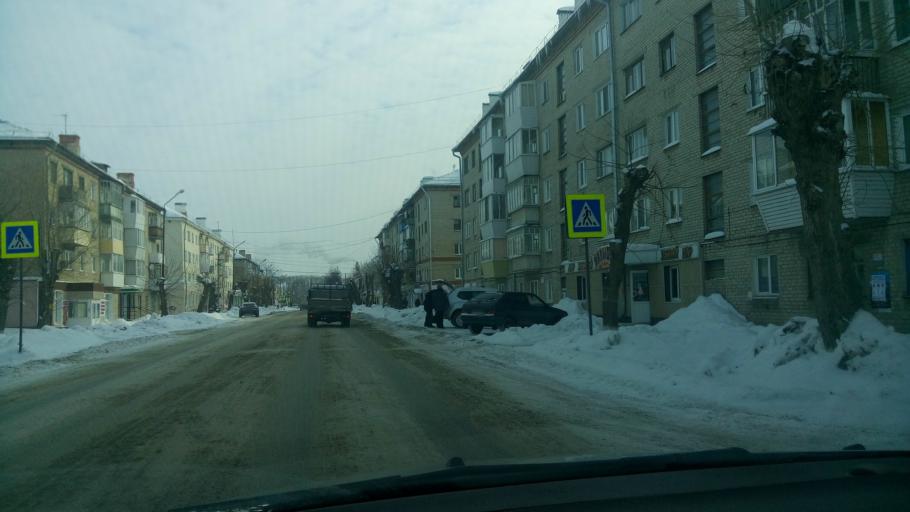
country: RU
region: Sverdlovsk
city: Bogdanovich
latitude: 56.7738
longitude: 62.0484
